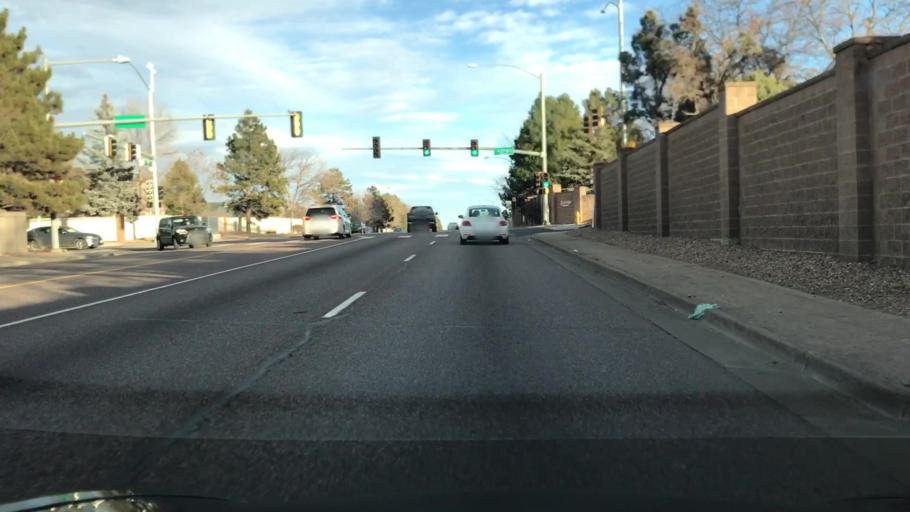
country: US
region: Colorado
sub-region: Adams County
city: Aurora
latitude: 39.6748
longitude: -104.8572
